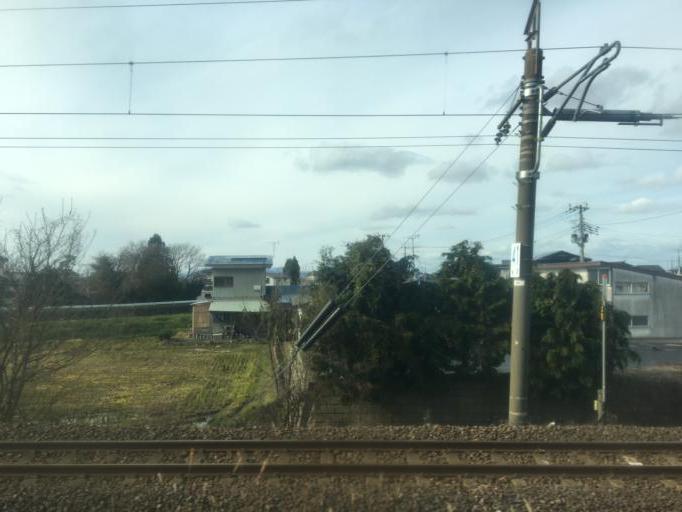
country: JP
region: Akita
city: Tenno
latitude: 39.9169
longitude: 140.0766
